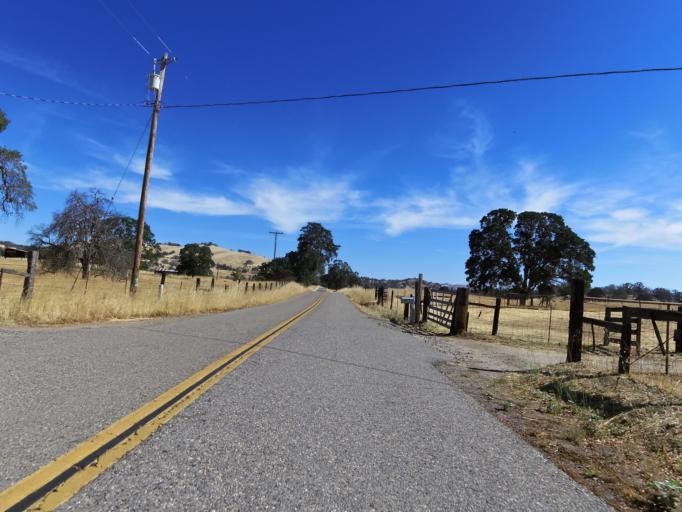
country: US
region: California
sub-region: Madera County
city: Yosemite Lakes
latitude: 37.2594
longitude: -119.9747
